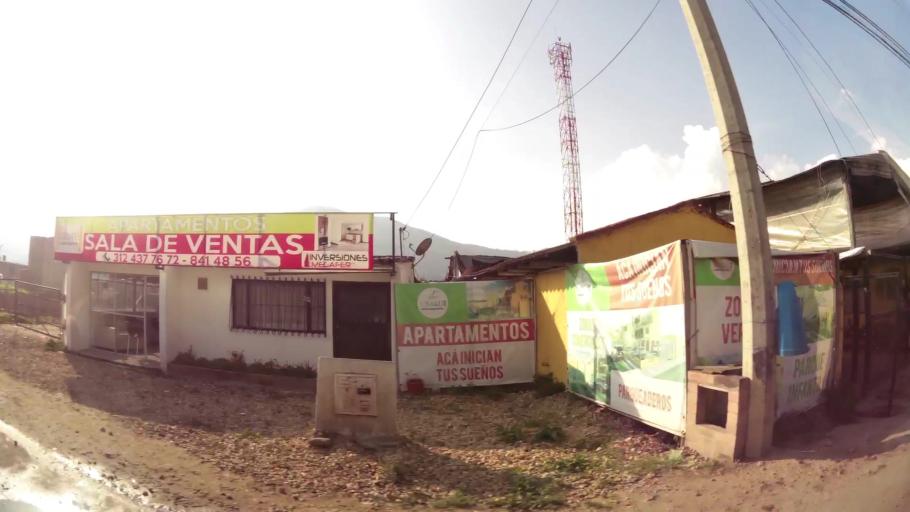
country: CO
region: Cundinamarca
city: Cota
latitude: 4.8027
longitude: -74.1013
